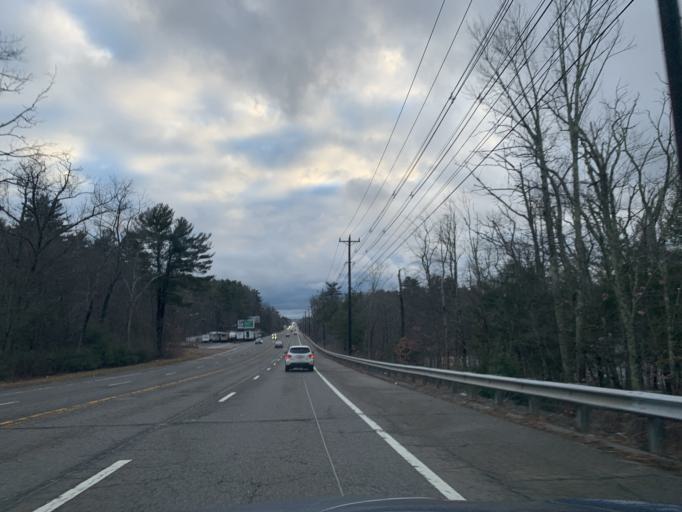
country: US
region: Massachusetts
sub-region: Norfolk County
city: Wrentham
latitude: 42.0677
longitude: -71.2928
